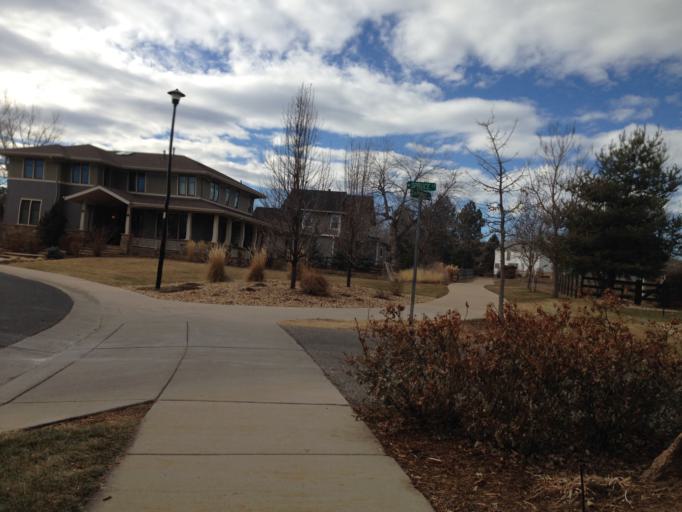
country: US
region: Colorado
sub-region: Boulder County
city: Louisville
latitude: 39.9778
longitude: -105.1456
